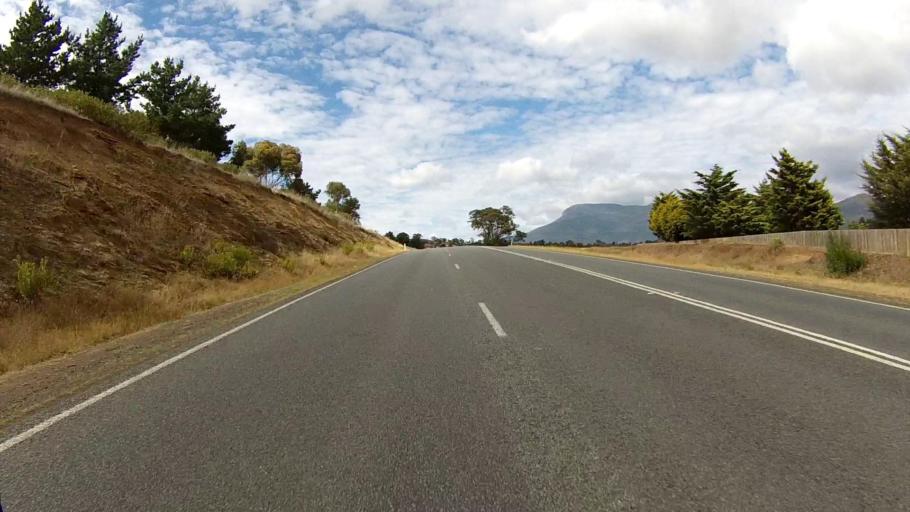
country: AU
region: Tasmania
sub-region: Brighton
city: Old Beach
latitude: -42.7915
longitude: 147.2932
